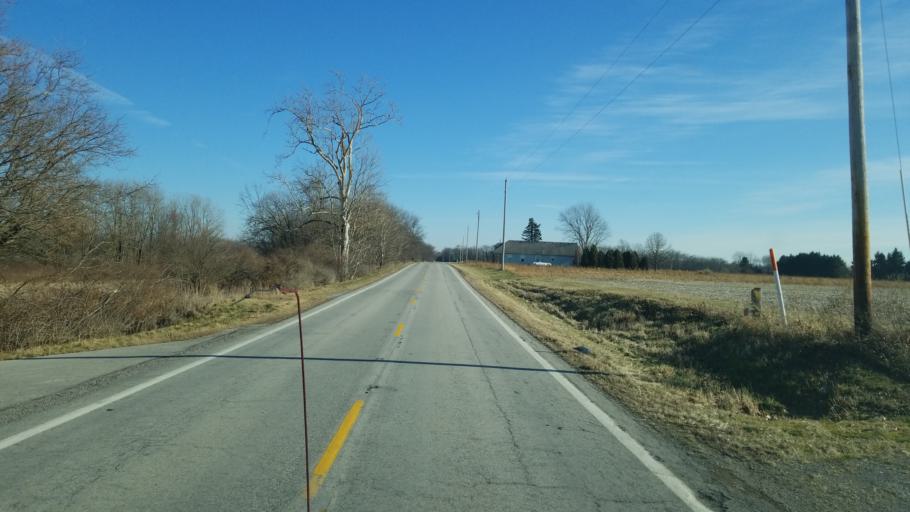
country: US
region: Ohio
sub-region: Henry County
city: Liberty Center
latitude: 41.4152
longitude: -83.9472
